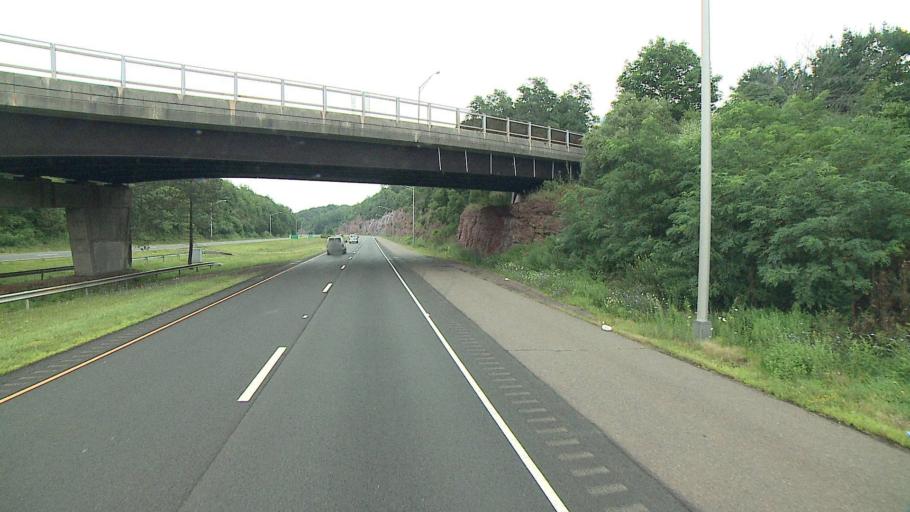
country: US
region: Connecticut
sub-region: New Haven County
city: Hamden
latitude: 41.3919
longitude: -72.8867
